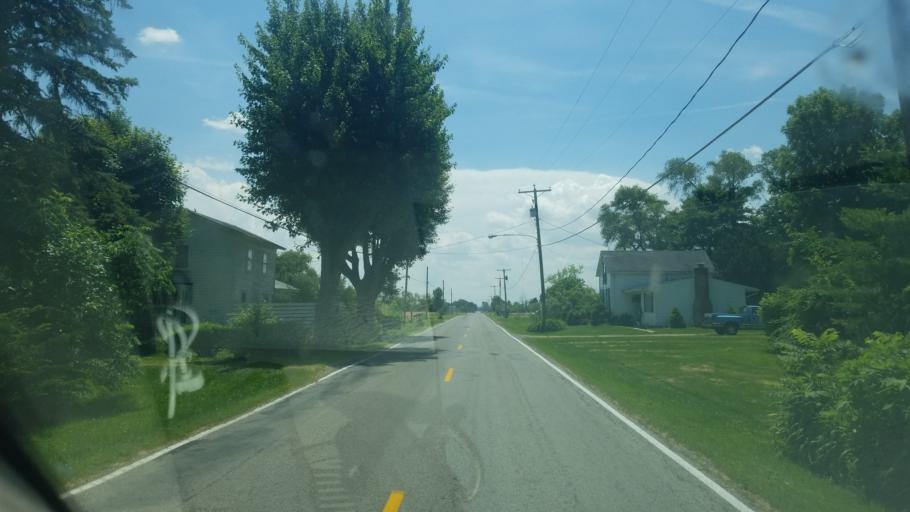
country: US
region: Ohio
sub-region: Hancock County
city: Arlington
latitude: 40.9331
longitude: -83.5945
